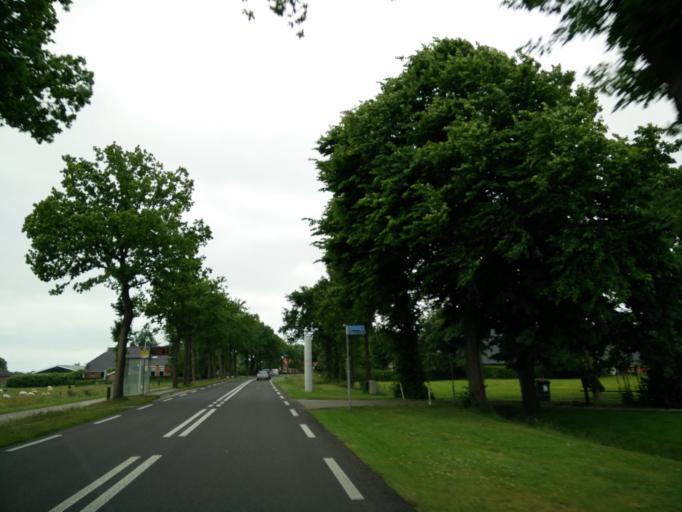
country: NL
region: Groningen
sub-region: Gemeente Groningen
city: Groningen
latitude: 53.1630
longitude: 6.4963
